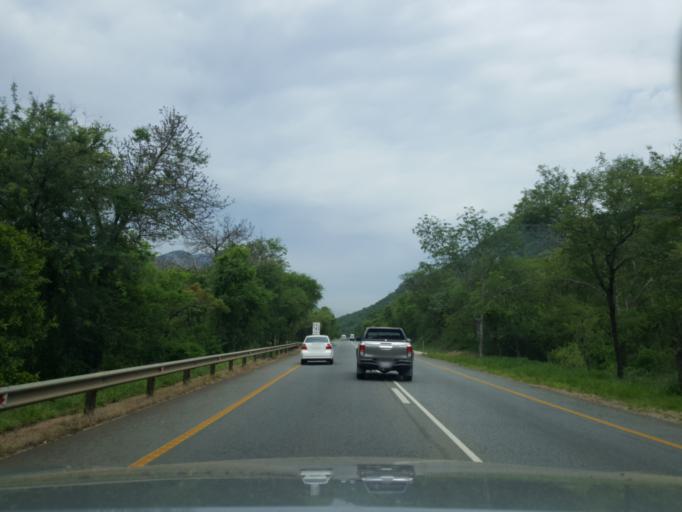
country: SZ
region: Hhohho
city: Ntfonjeni
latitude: -25.5289
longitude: 31.2809
